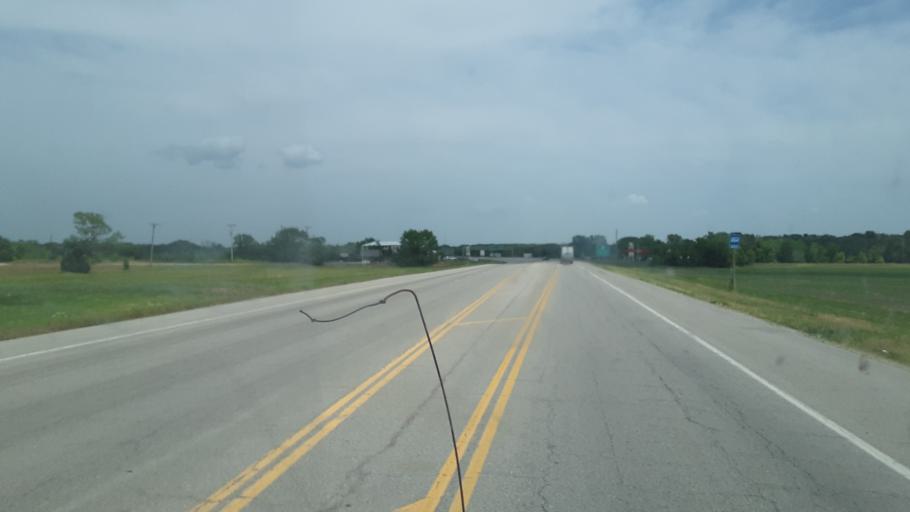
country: US
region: Kansas
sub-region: Bourbon County
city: Fort Scott
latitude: 37.8562
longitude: -94.7171
